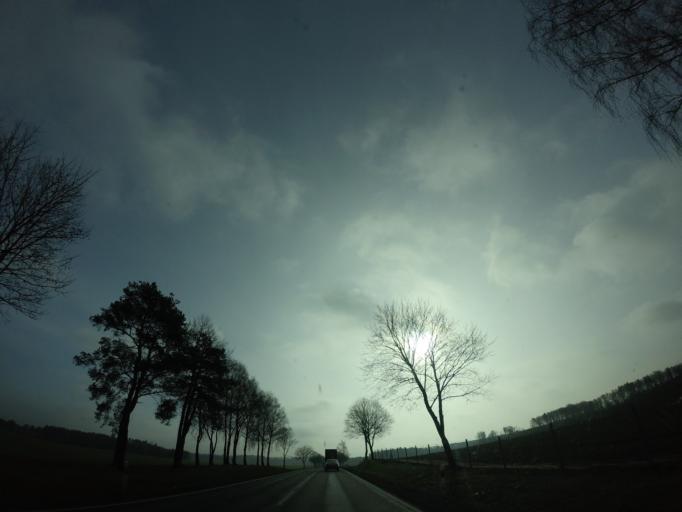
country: PL
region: West Pomeranian Voivodeship
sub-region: Powiat walecki
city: Walcz
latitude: 53.3192
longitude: 16.3241
